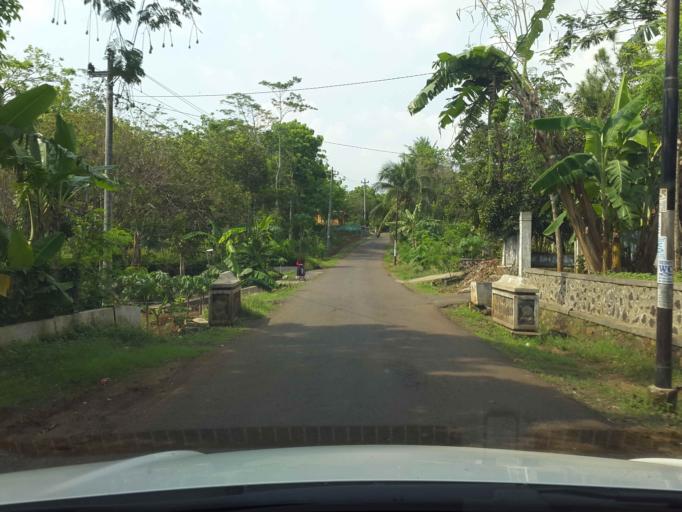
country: ID
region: Central Java
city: Karanganyar
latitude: -7.3219
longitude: 108.6463
